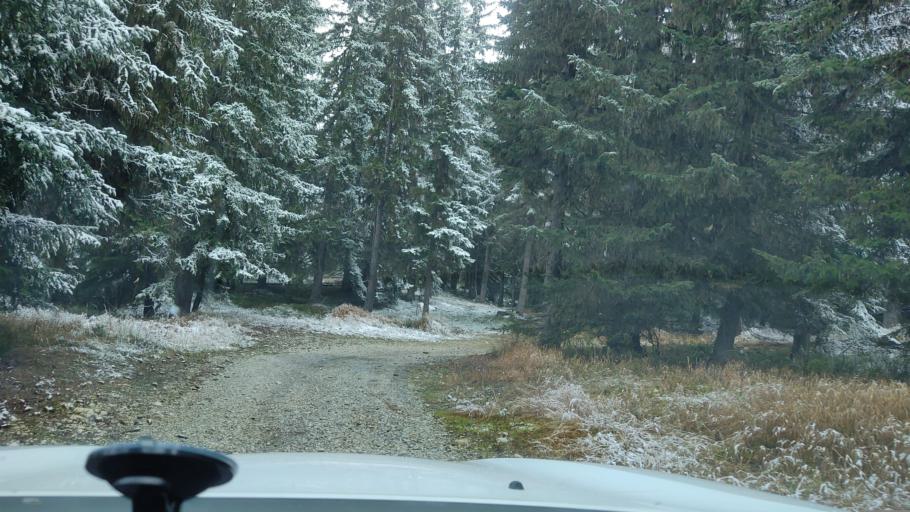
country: FR
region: Rhone-Alpes
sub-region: Departement de la Savoie
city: Seez
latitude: 45.5975
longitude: 6.8075
